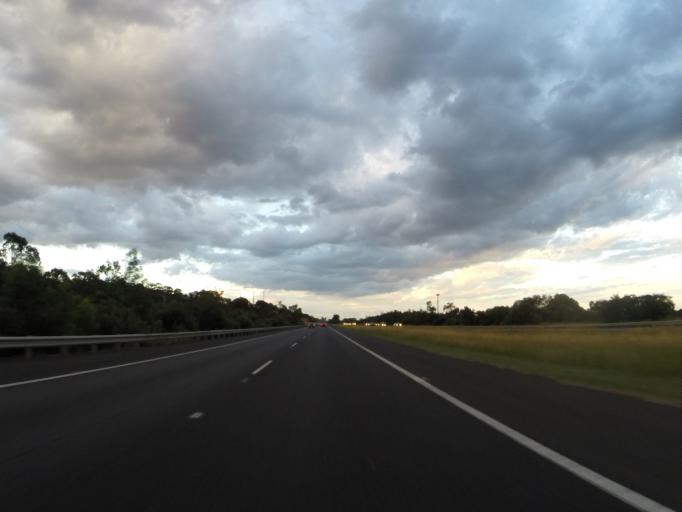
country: AU
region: New South Wales
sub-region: Campbelltown Municipality
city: Glen Alpine
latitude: -34.0781
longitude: 150.7738
